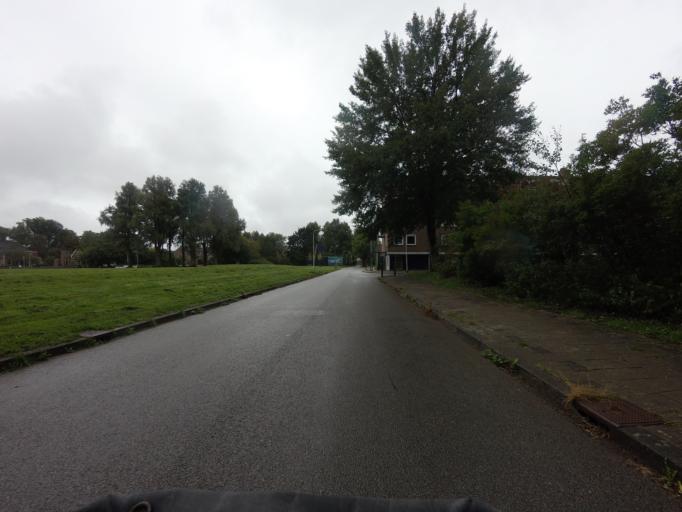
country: NL
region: Friesland
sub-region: Gemeente Leeuwarden
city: Bilgaard
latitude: 53.2175
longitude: 5.8055
